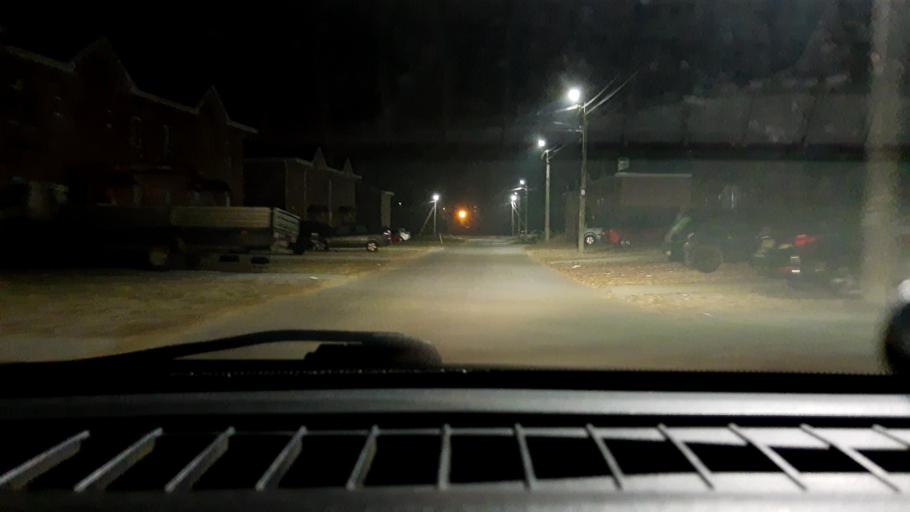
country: RU
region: Nizjnij Novgorod
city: Afonino
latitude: 56.2105
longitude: 44.0911
